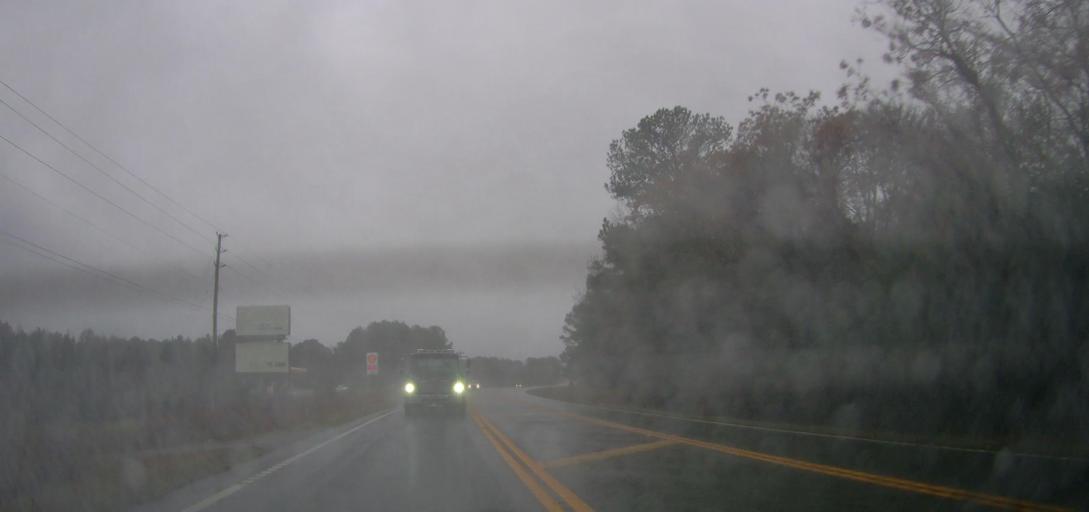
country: US
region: Georgia
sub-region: Jones County
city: Gray
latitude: 33.0778
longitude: -83.4837
